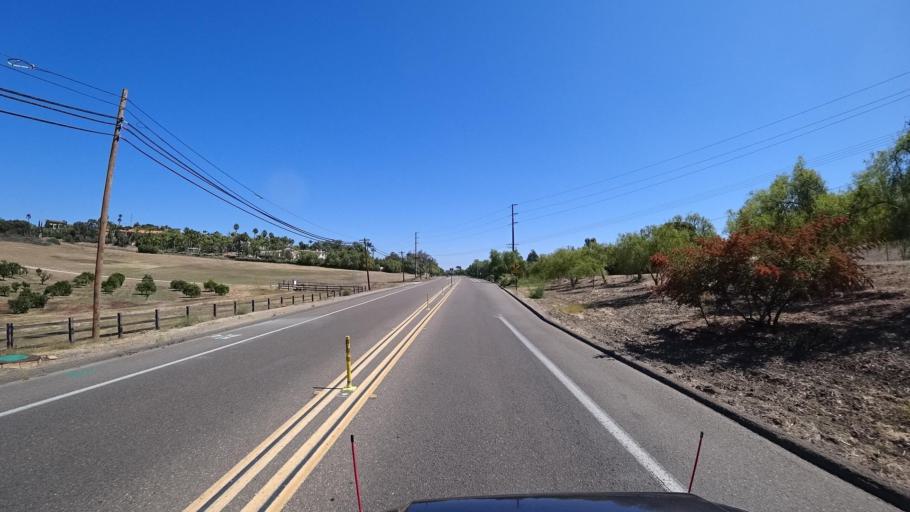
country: US
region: California
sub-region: San Diego County
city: Rancho Santa Fe
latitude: 33.0353
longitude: -117.1778
